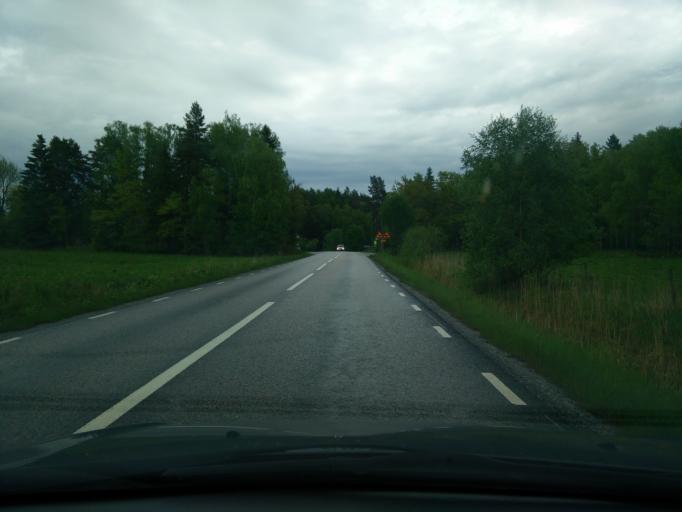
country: SE
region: Stockholm
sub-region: Norrtalje Kommun
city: Norrtalje
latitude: 59.7823
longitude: 18.8348
